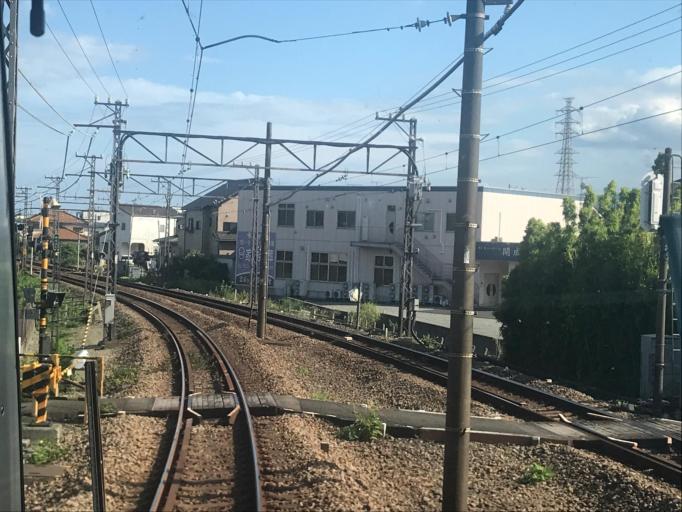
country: JP
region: Kanagawa
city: Hadano
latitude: 35.3437
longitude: 139.1372
